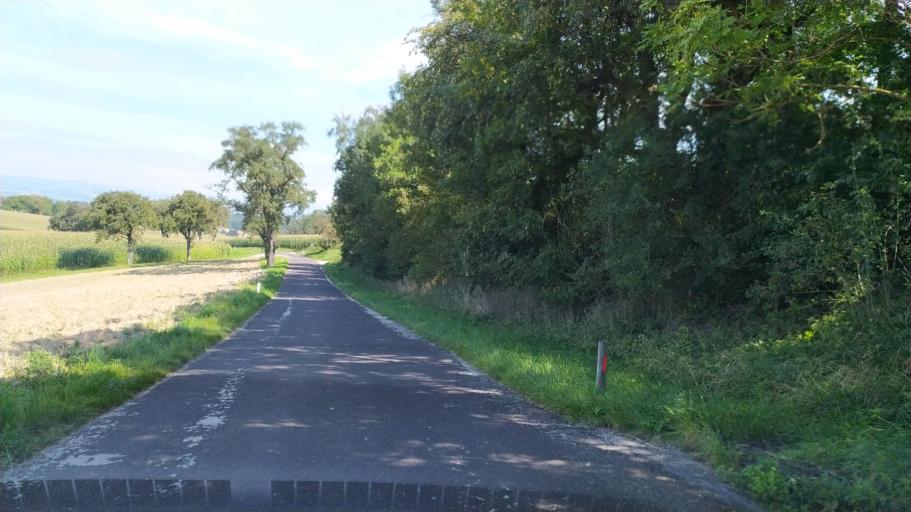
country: AT
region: Lower Austria
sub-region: Politischer Bezirk Amstetten
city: Strengberg
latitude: 48.1411
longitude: 14.6136
